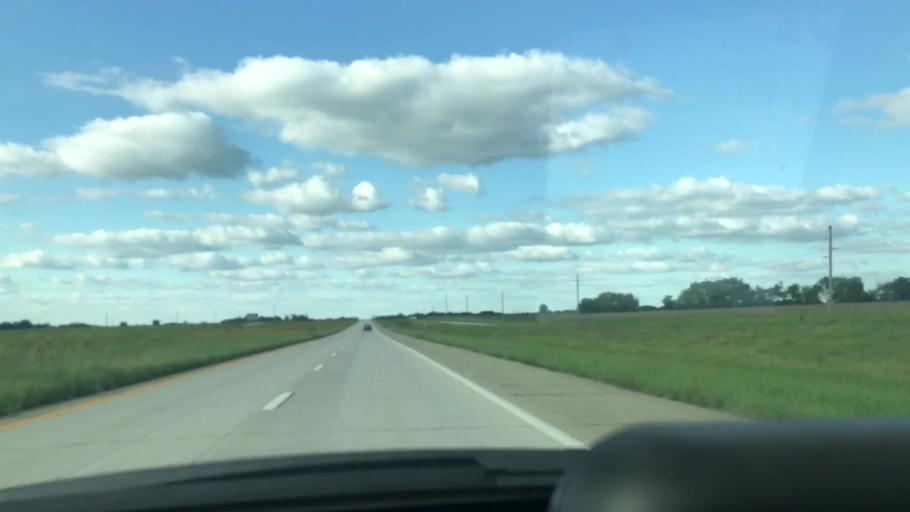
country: US
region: Missouri
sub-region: Benton County
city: Cole Camp
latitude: 38.5108
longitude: -93.2727
